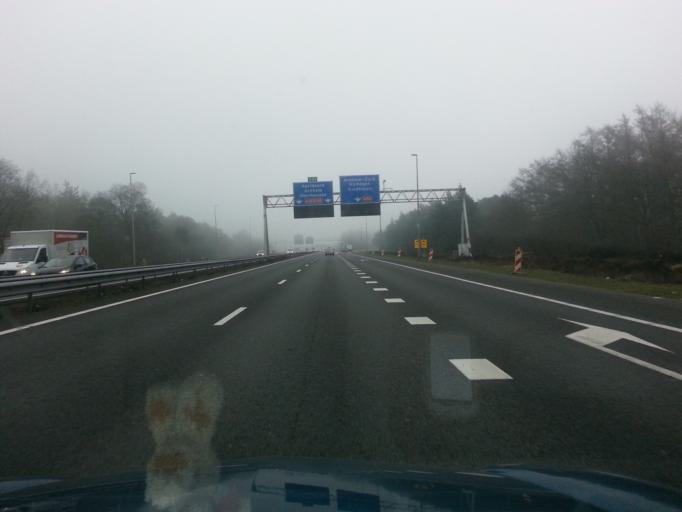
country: NL
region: Gelderland
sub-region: Gemeente Renkum
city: Wolfheze
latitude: 52.0236
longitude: 5.8090
